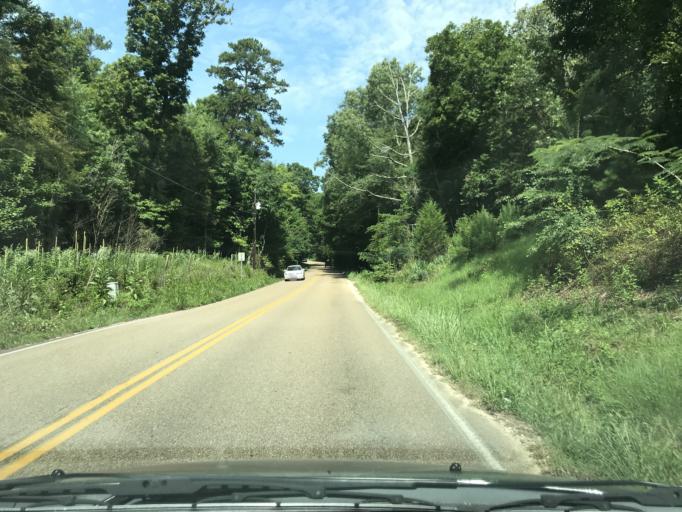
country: US
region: Tennessee
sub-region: Hamilton County
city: Lakesite
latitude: 35.1675
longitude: -85.0673
